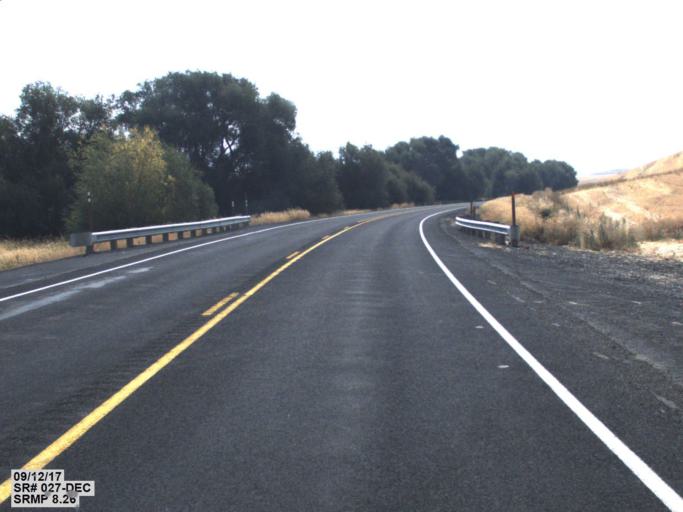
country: US
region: Washington
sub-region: Whitman County
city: Pullman
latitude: 46.8343
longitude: -117.1172
